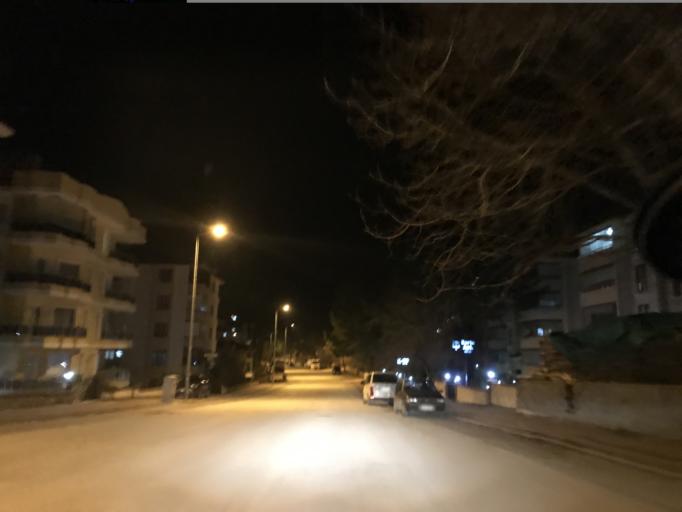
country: TR
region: Karabuk
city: Safranbolu
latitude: 41.2571
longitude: 32.6807
